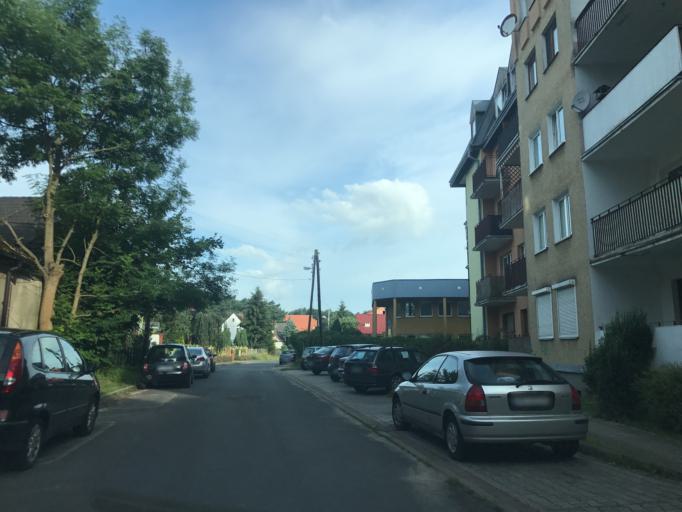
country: PL
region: West Pomeranian Voivodeship
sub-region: Powiat goleniowski
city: Goleniow
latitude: 53.5592
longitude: 14.8209
